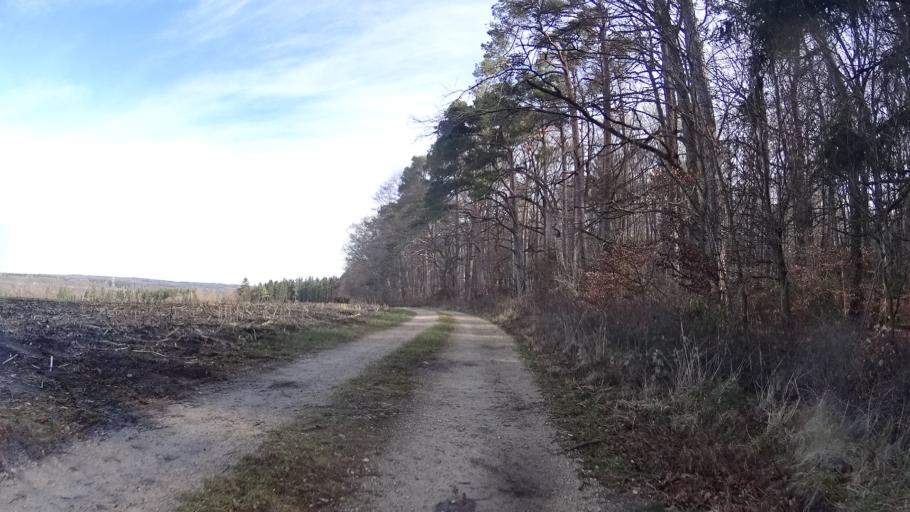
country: DE
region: Bavaria
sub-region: Upper Bavaria
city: Walting
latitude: 48.8877
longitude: 11.2775
